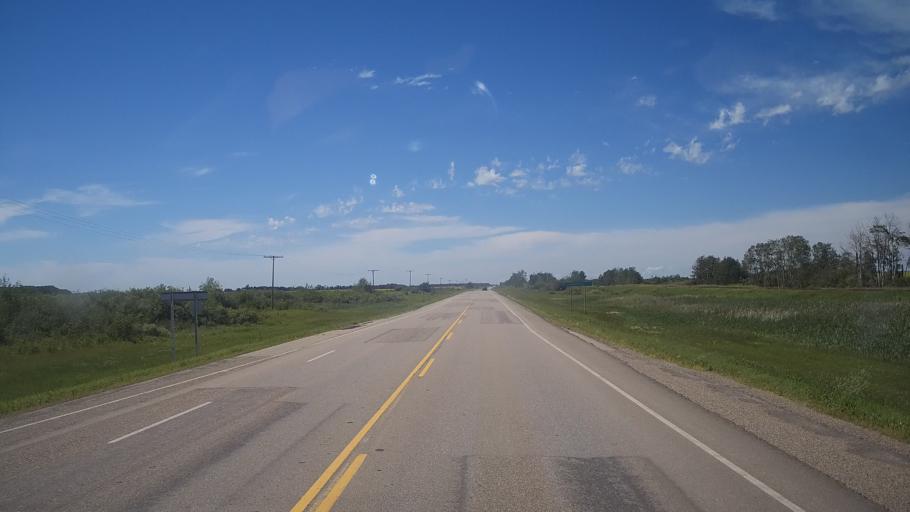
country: CA
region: Saskatchewan
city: Langenburg
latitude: 50.8015
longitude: -101.5803
